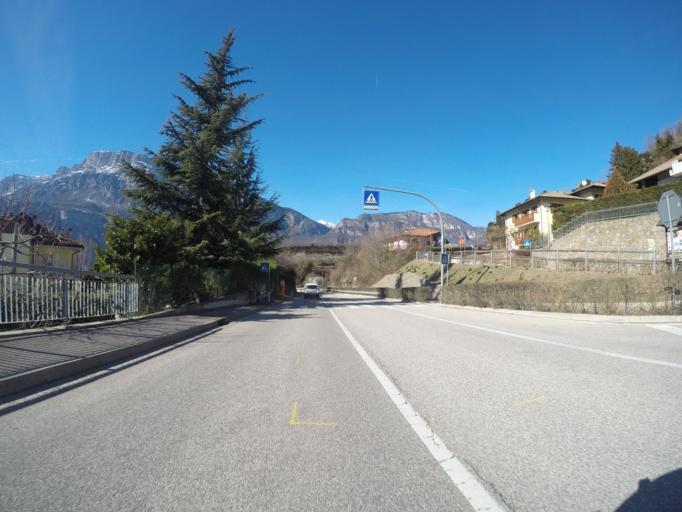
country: IT
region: Trentino-Alto Adige
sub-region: Provincia di Trento
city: Lavis
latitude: 46.1450
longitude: 11.1118
